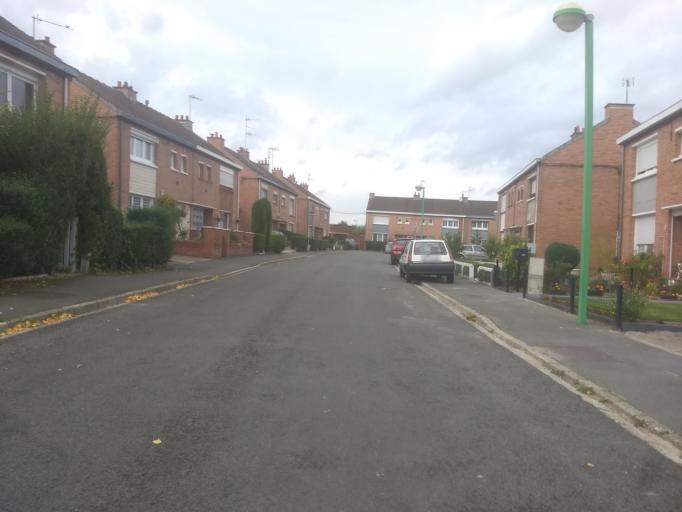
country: FR
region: Nord-Pas-de-Calais
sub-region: Departement du Pas-de-Calais
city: Achicourt
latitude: 50.2725
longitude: 2.7658
